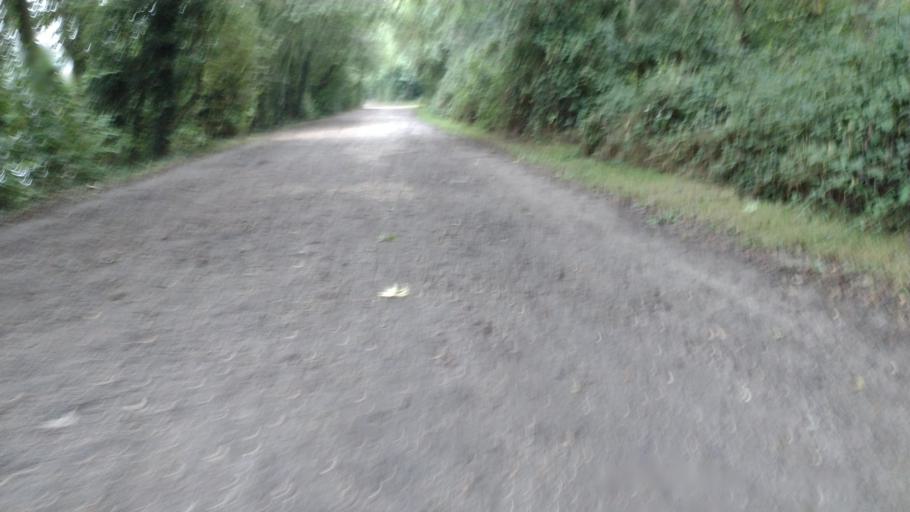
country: GB
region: England
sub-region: Wokingham
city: Woodley
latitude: 51.4412
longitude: -0.8845
